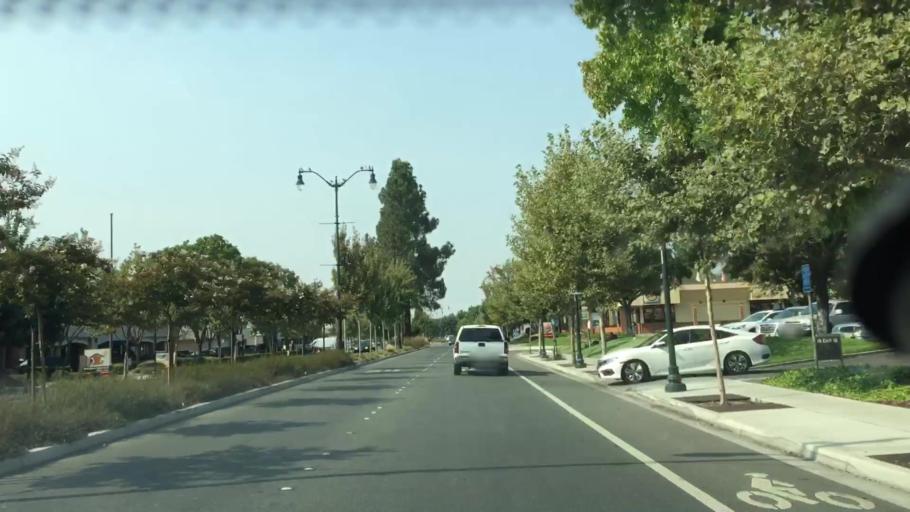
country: US
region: California
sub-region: Contra Costa County
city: Pacheco
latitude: 37.9718
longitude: -122.0636
